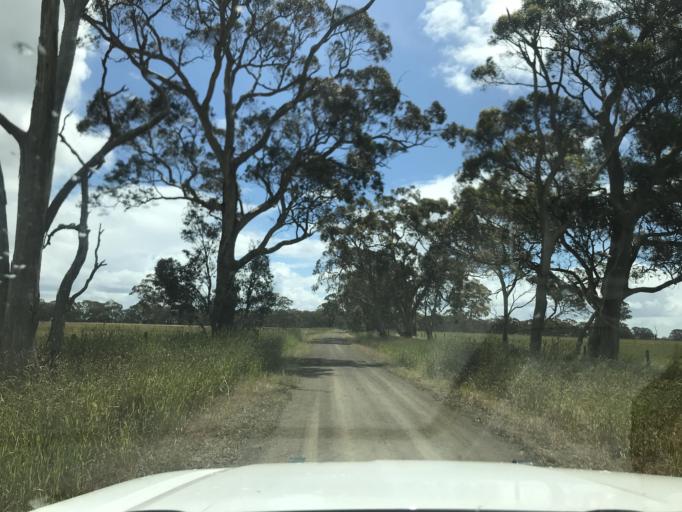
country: AU
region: South Australia
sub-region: Wattle Range
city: Penola
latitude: -37.1255
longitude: 141.3017
